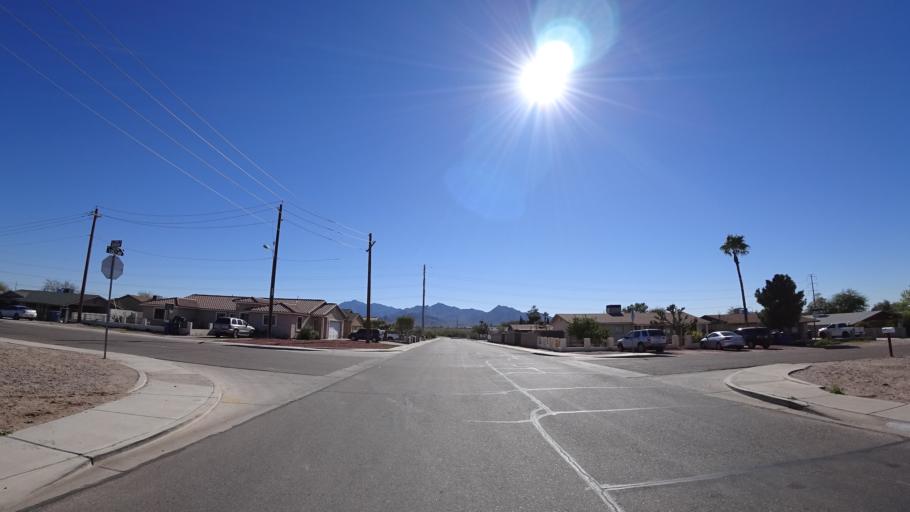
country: US
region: Arizona
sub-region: Maricopa County
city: Avondale
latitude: 33.4135
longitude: -112.3278
